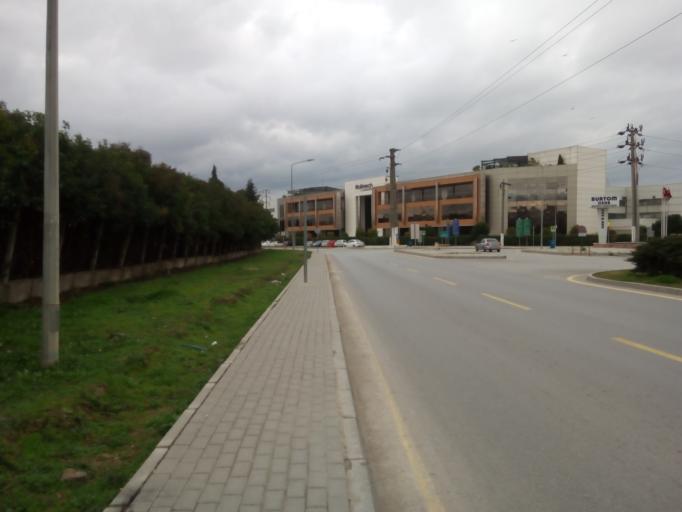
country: TR
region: Bursa
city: Niluefer
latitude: 40.2481
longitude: 28.9558
